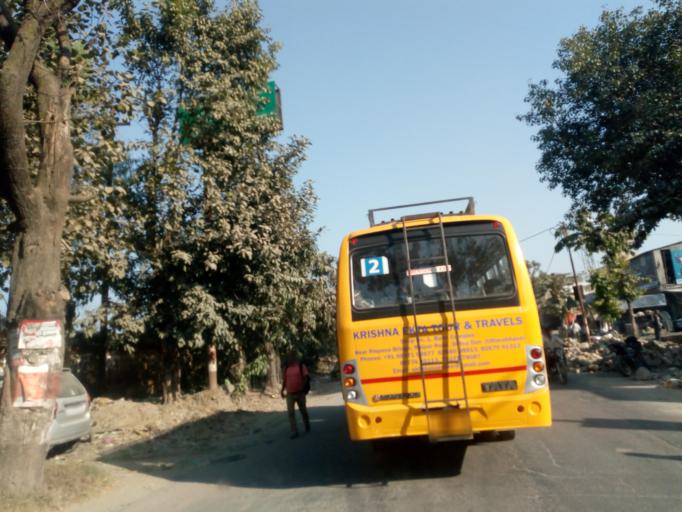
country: IN
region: Uttarakhand
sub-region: Dehradun
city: Vikasnagar
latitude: 30.3510
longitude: 77.8652
